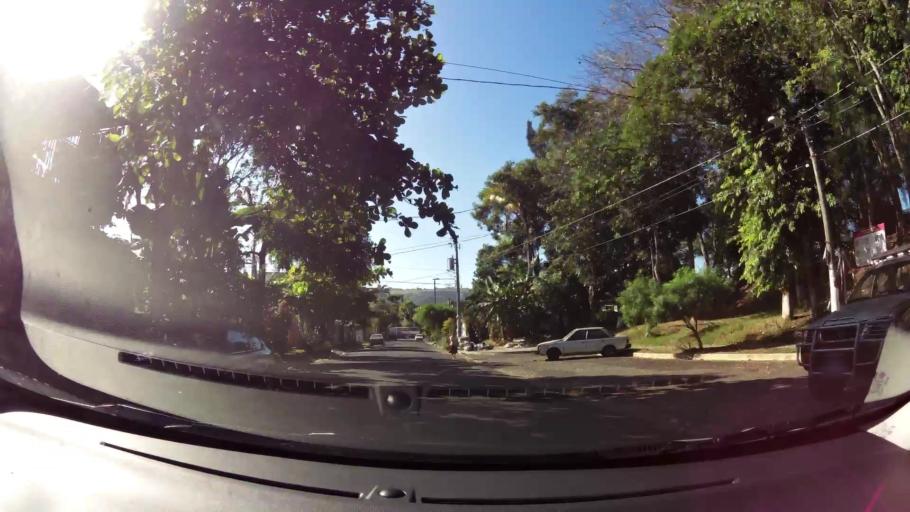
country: SV
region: La Libertad
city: Santa Tecla
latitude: 13.6853
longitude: -89.2933
